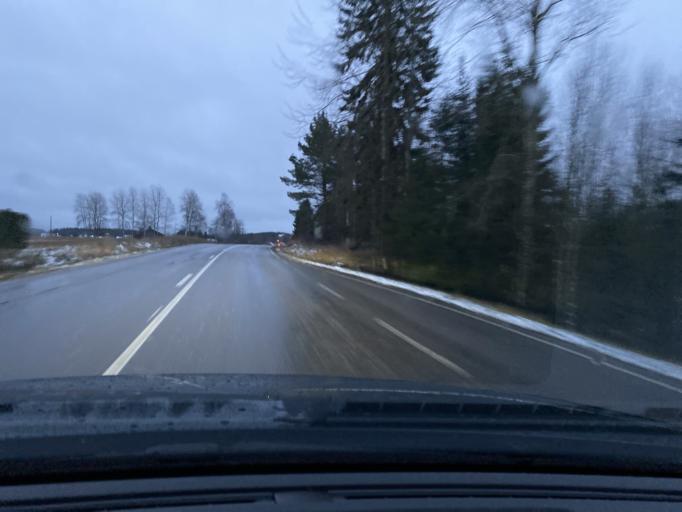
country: FI
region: Pirkanmaa
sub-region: Lounais-Pirkanmaa
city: Punkalaidun
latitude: 61.1214
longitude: 23.0585
